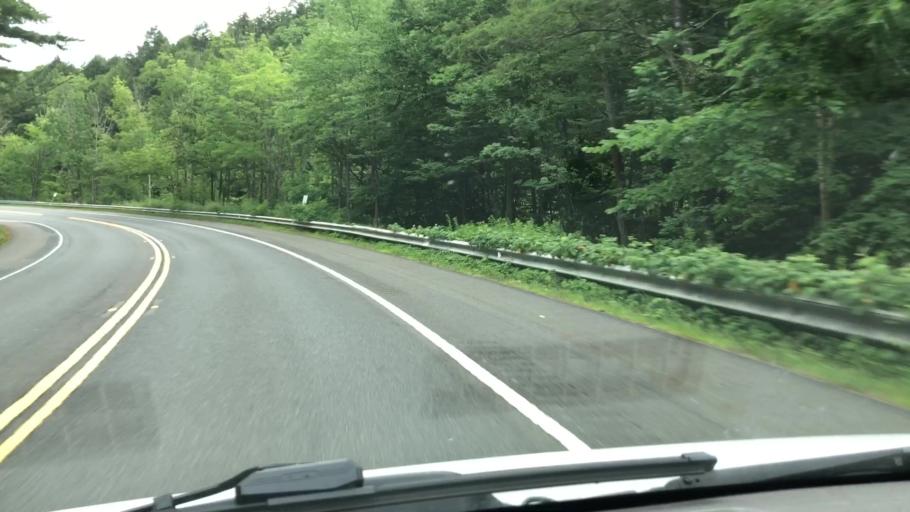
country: US
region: Massachusetts
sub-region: Hampshire County
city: Chesterfield
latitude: 42.4404
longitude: -72.8679
